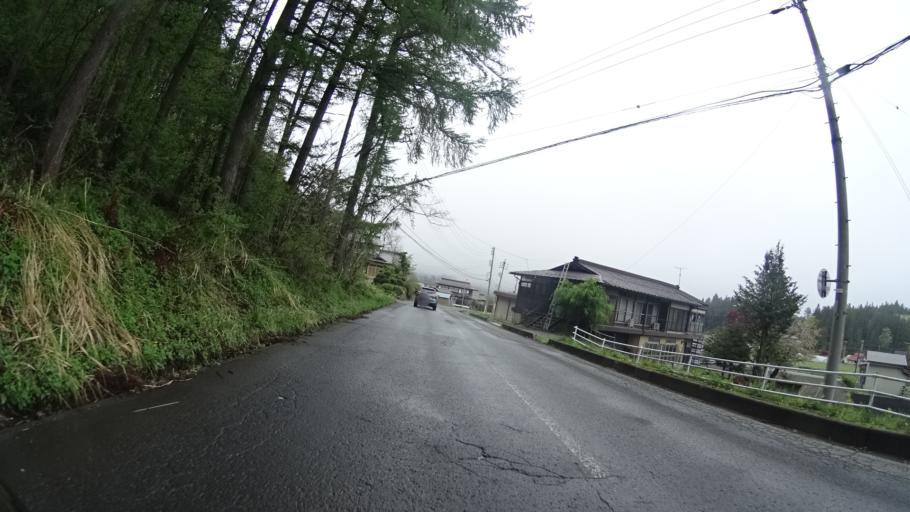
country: JP
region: Nagano
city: Nagano-shi
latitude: 36.7672
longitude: 138.1992
